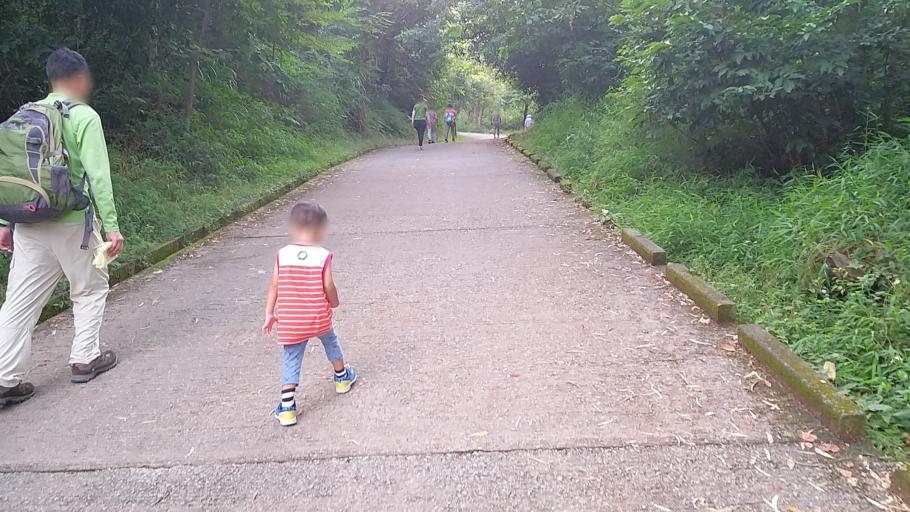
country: HK
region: Tuen Mun
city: Tuen Mun
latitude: 22.4045
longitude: 113.9572
